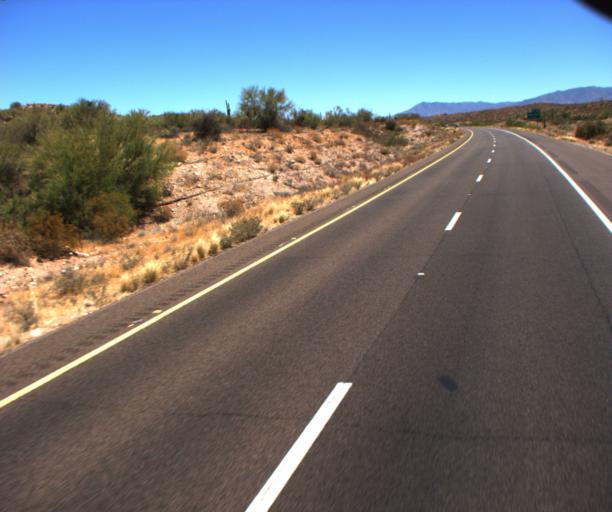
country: US
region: Arizona
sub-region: Maricopa County
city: Fountain Hills
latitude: 33.6102
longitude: -111.5747
